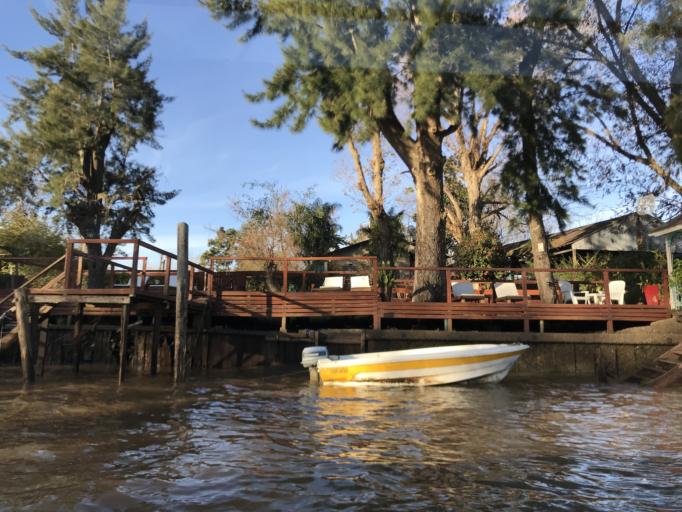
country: AR
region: Buenos Aires
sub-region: Partido de Tigre
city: Tigre
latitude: -34.4039
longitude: -58.5940
